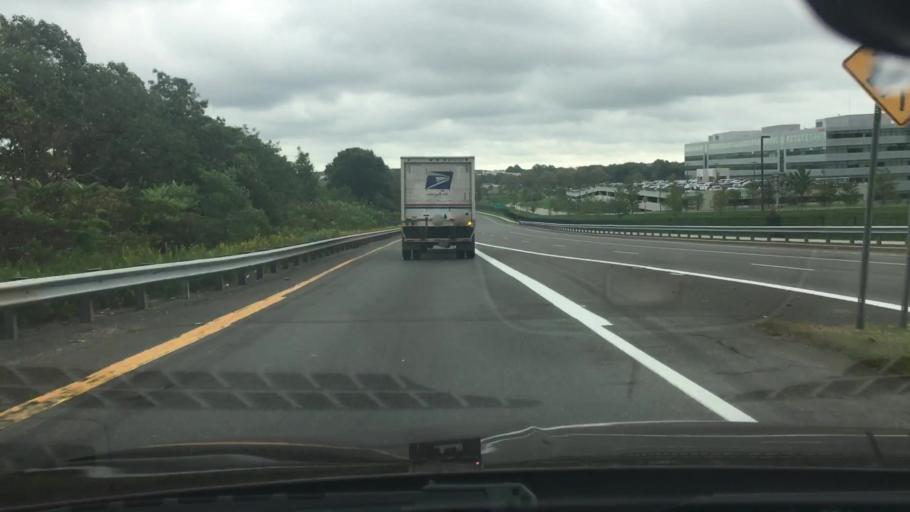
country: US
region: New York
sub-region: Suffolk County
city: Melville
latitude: 40.7817
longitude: -73.4316
